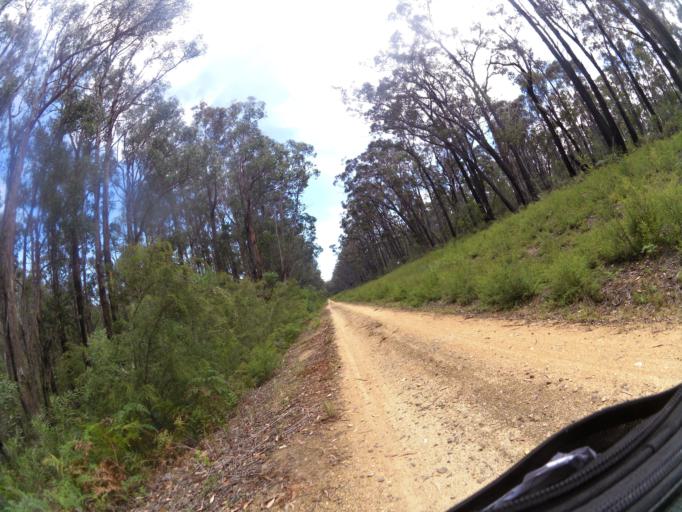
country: AU
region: Victoria
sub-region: East Gippsland
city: Lakes Entrance
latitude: -37.7403
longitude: 148.0124
